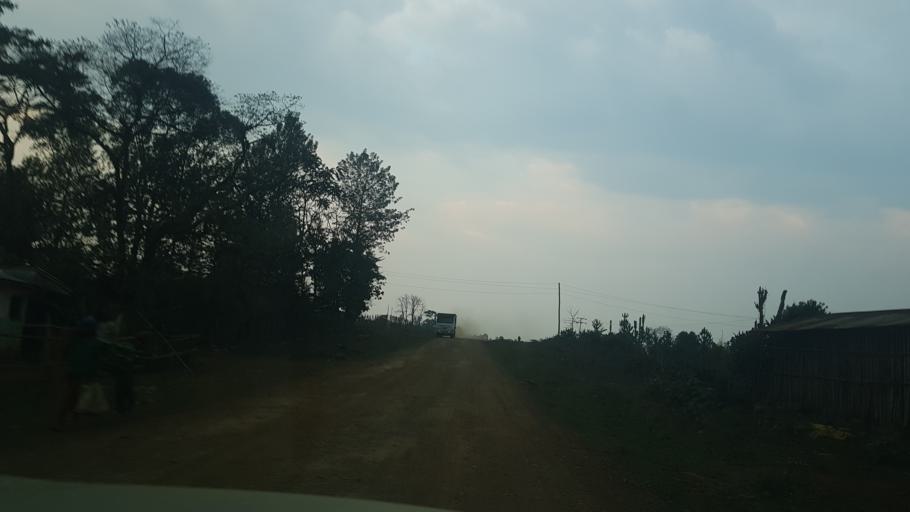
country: ET
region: Oromiya
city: Gore
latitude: 7.9159
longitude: 35.5138
